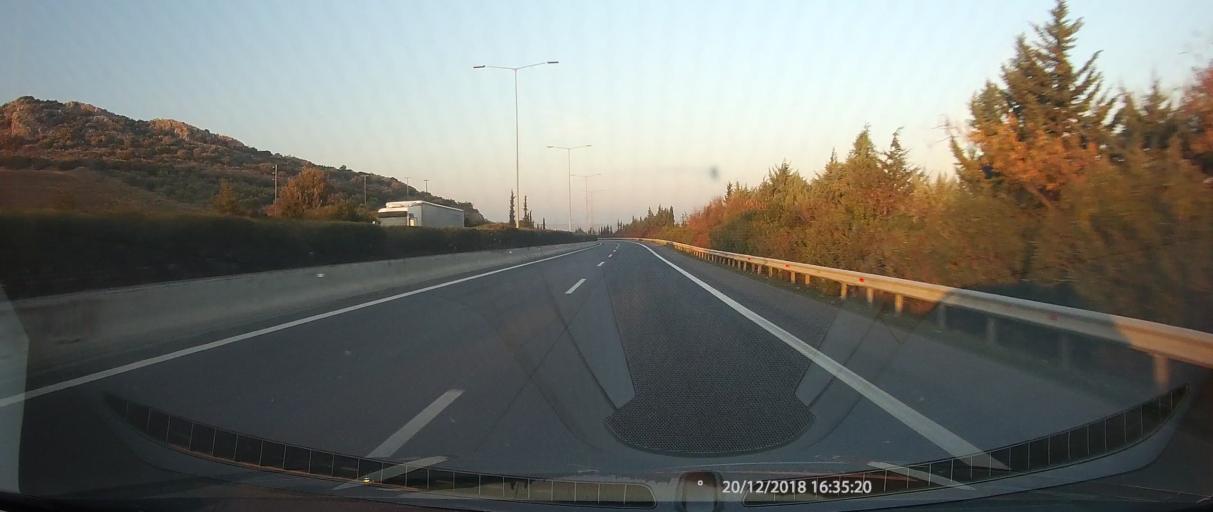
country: GR
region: Thessaly
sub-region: Nomos Magnisias
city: Nea Anchialos
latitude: 39.3013
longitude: 22.7473
